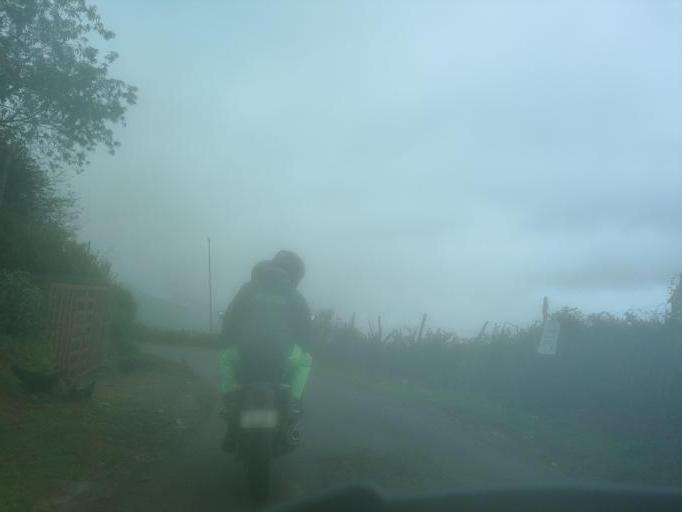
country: IN
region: Tamil Nadu
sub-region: Dindigul
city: Kodaikanal
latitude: 10.2053
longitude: 77.3411
